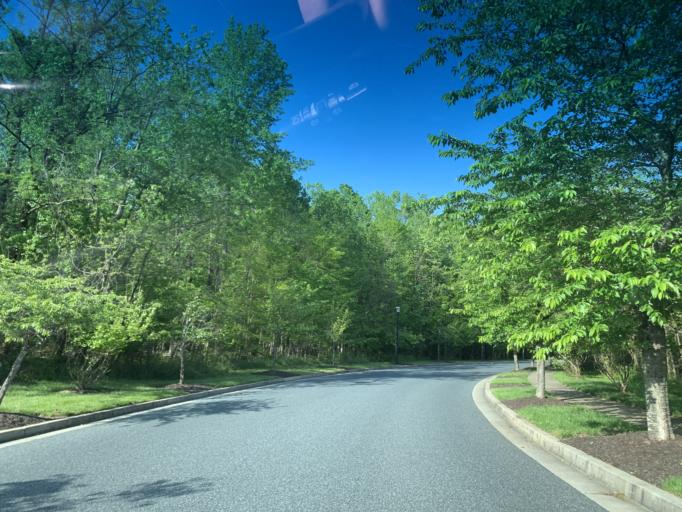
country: US
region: Maryland
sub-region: Baltimore County
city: White Marsh
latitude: 39.4003
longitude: -76.4331
